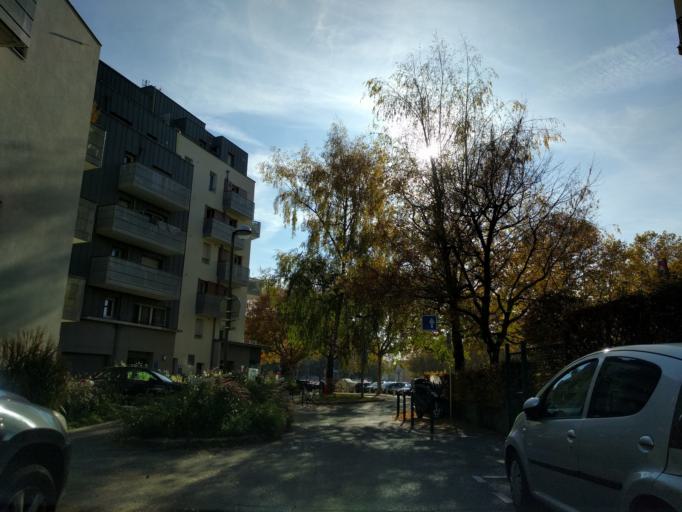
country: FR
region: Rhone-Alpes
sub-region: Departement de la Haute-Savoie
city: Annecy
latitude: 45.9090
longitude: 6.1226
